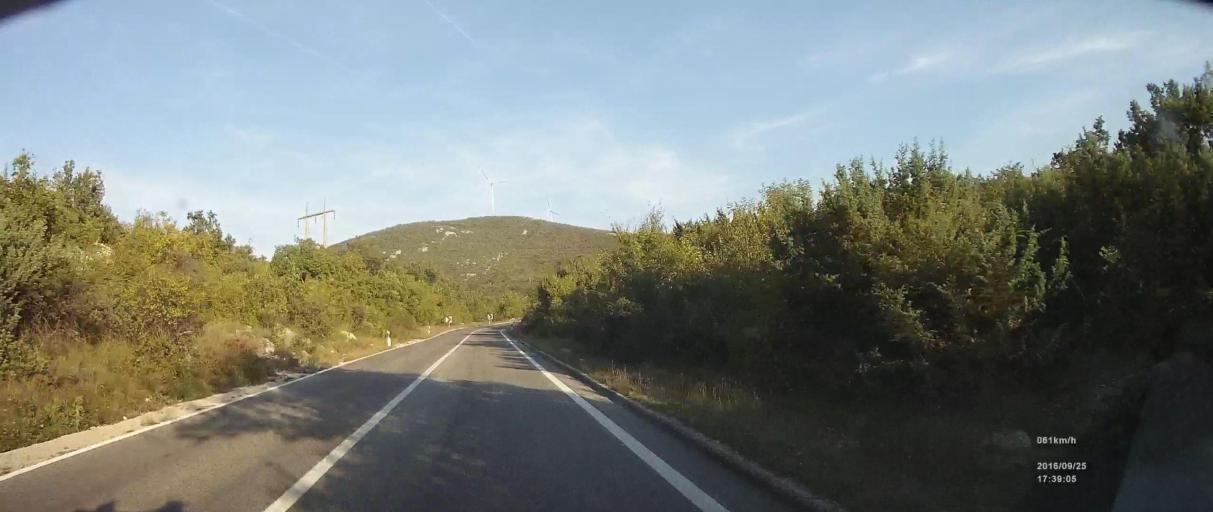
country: HR
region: Sibensko-Kniniska
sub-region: Grad Sibenik
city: Brodarica
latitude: 43.6473
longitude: 16.0594
